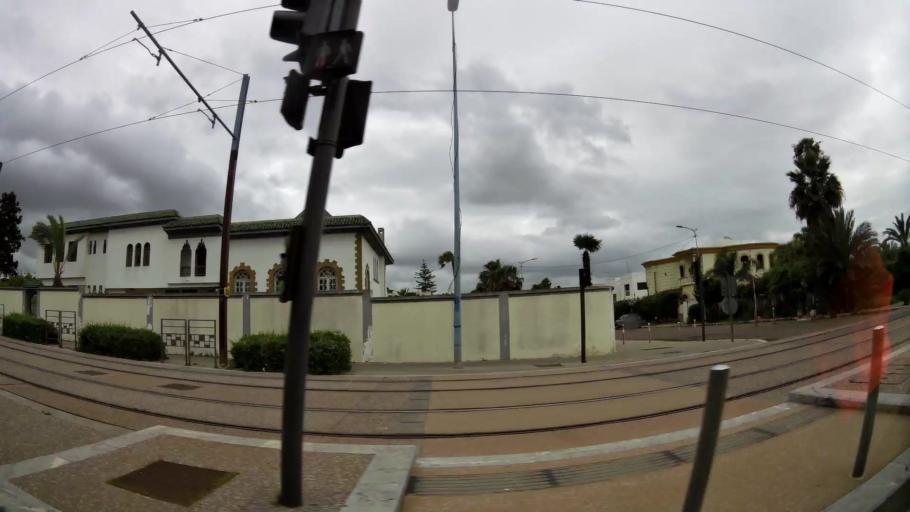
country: MA
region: Grand Casablanca
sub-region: Casablanca
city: Casablanca
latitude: 33.5459
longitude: -7.6364
